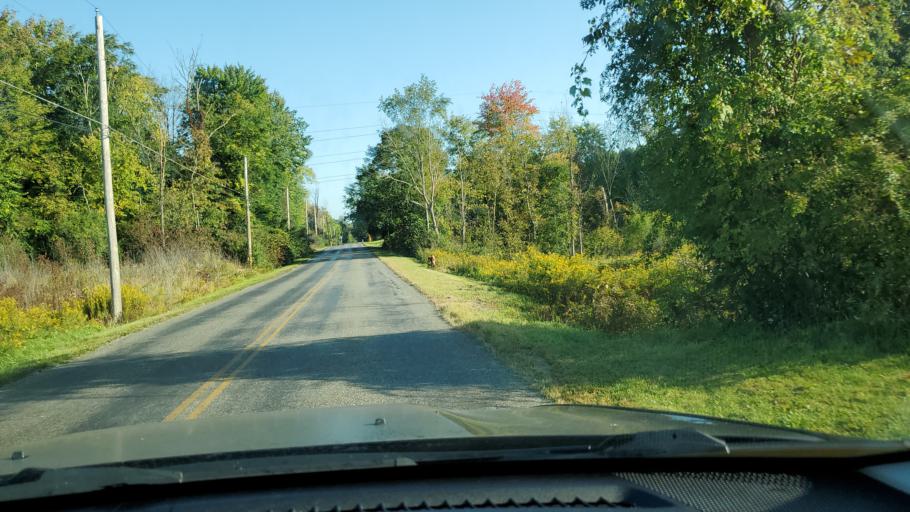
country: US
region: Ohio
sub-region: Trumbull County
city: Niles
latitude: 41.1623
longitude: -80.7535
